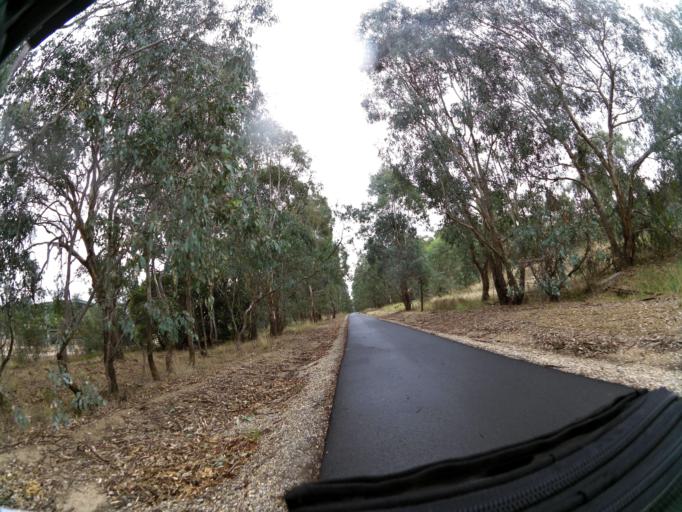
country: AU
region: Victoria
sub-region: Wodonga
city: Wodonga
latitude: -36.1429
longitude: 146.9153
